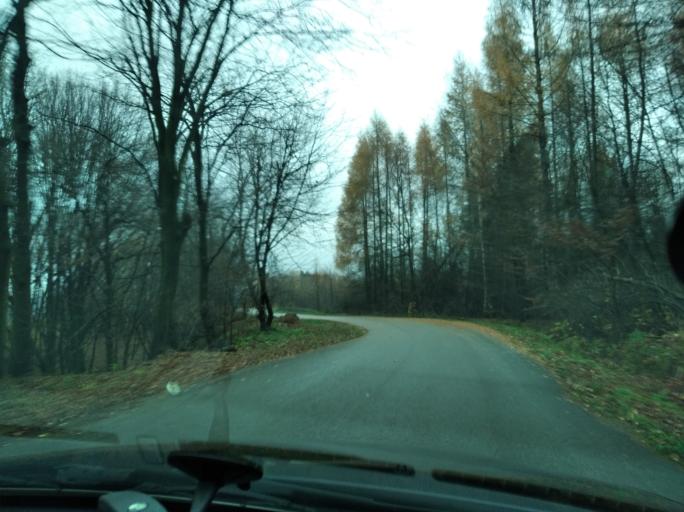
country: PL
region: Subcarpathian Voivodeship
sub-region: Powiat przeworski
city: Jawornik Polski
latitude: 49.9022
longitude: 22.2767
